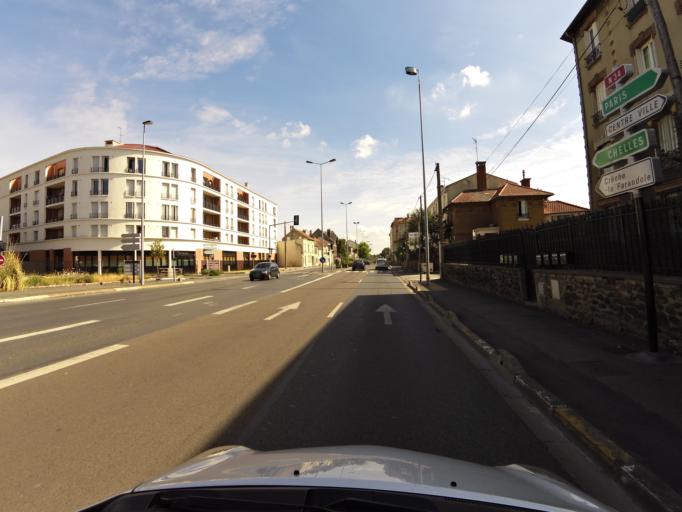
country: FR
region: Ile-de-France
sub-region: Departement de Seine-Saint-Denis
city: Neuilly-sur-Marne
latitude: 48.8593
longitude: 2.5370
